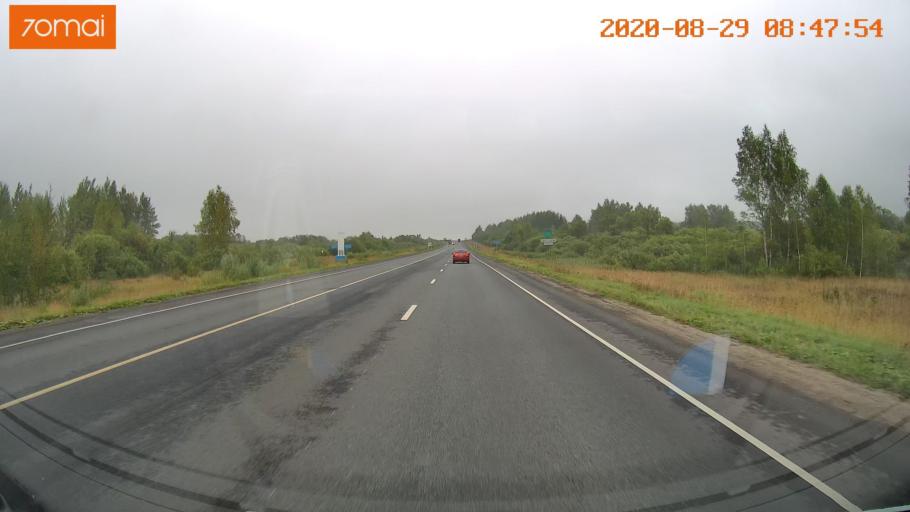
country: RU
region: Ivanovo
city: Vichuga
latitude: 57.1553
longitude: 41.8404
